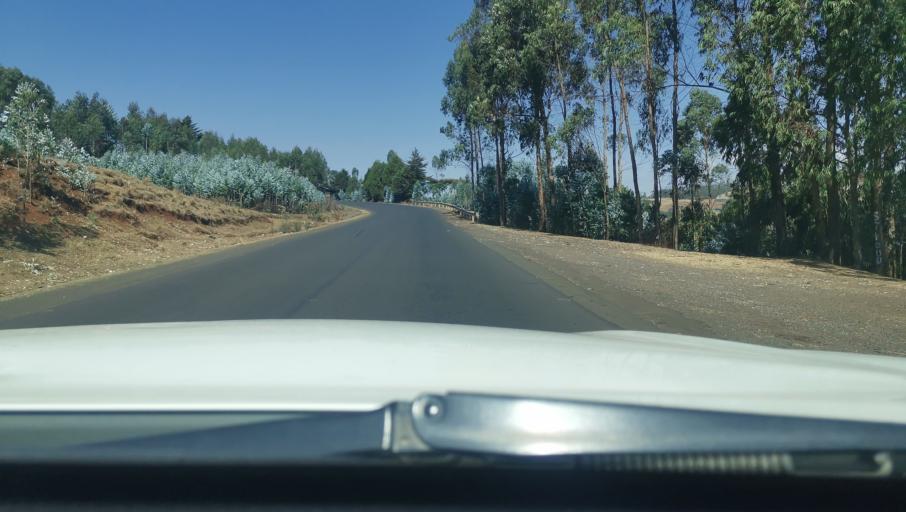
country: ET
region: Oromiya
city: Gedo
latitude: 8.9801
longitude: 37.4777
